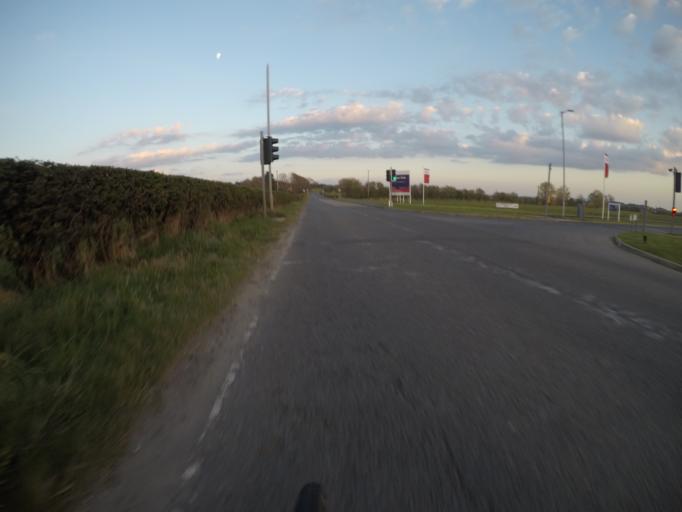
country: GB
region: Scotland
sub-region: South Ayrshire
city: Troon
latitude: 55.5580
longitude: -4.6284
